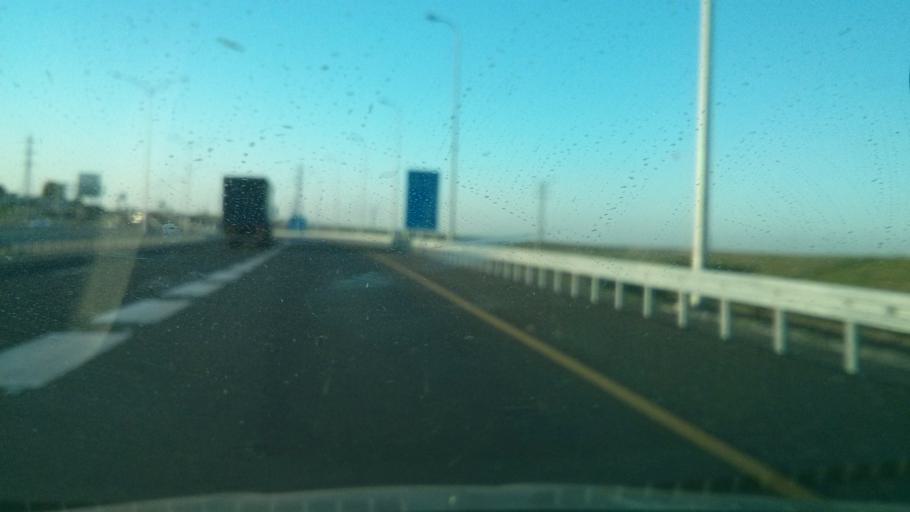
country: IL
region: Southern District
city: Lehavim
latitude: 31.4265
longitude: 34.7836
